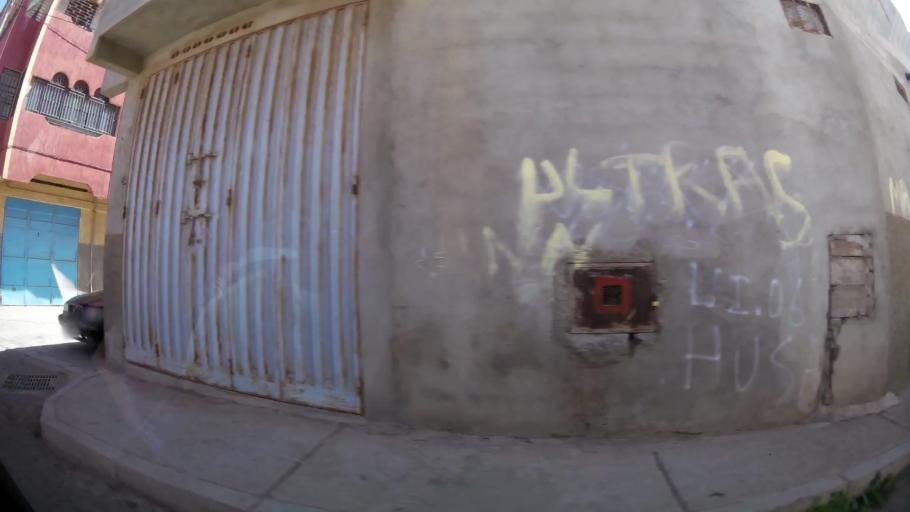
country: MA
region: Souss-Massa-Draa
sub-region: Inezgane-Ait Mellou
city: Inezgane
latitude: 30.3370
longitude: -9.5110
